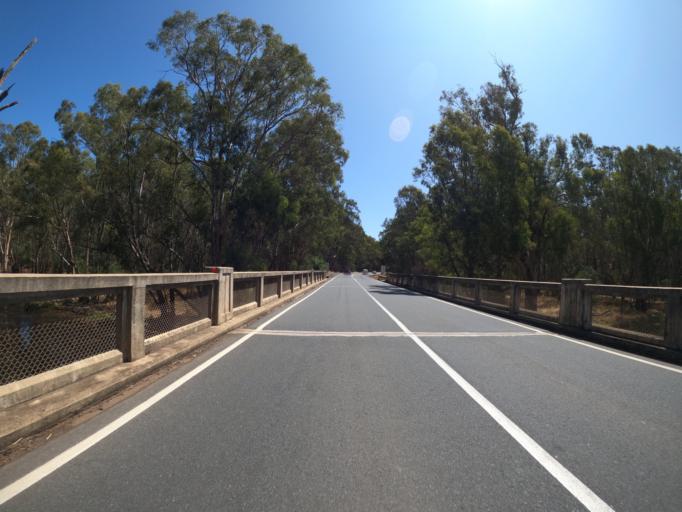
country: AU
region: New South Wales
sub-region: Corowa Shire
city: Corowa
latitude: -36.0689
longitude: 146.1992
